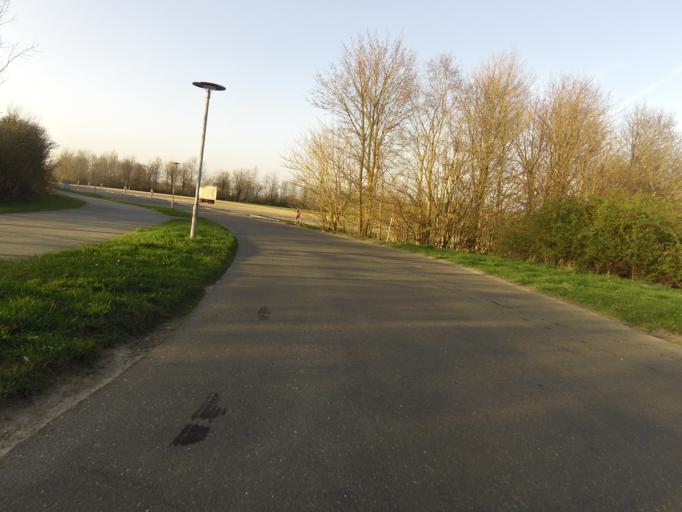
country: DK
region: South Denmark
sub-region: Vejen Kommune
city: Vejen
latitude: 55.4717
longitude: 9.1209
